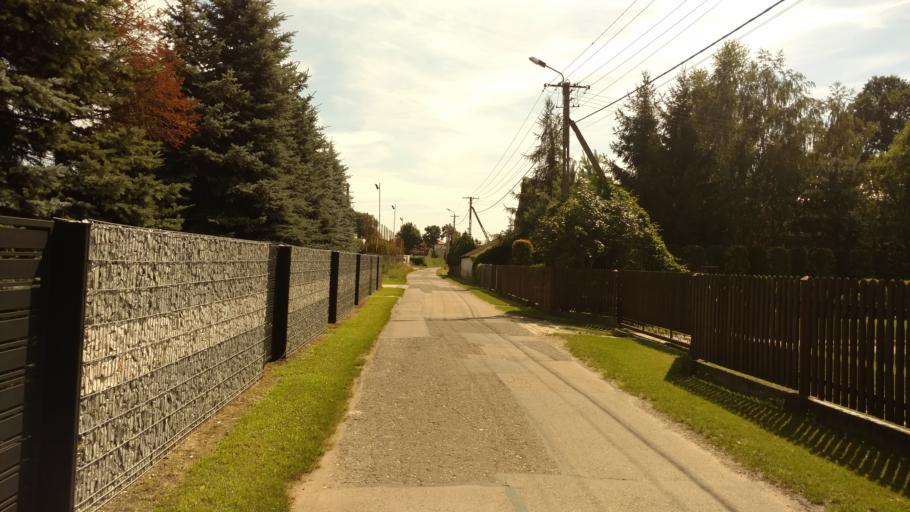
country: PL
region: Silesian Voivodeship
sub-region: Powiat pszczynski
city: Jankowice
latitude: 50.0026
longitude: 18.9827
